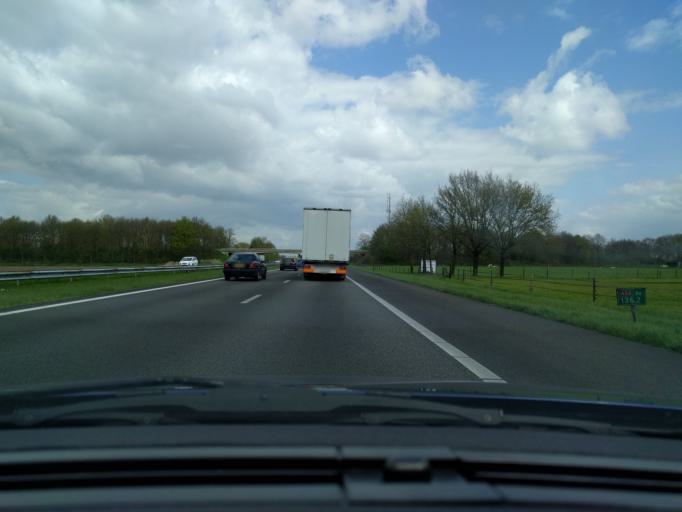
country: NL
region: North Brabant
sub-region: Gemeente Landerd
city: Schaijk
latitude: 51.7685
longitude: 5.6305
